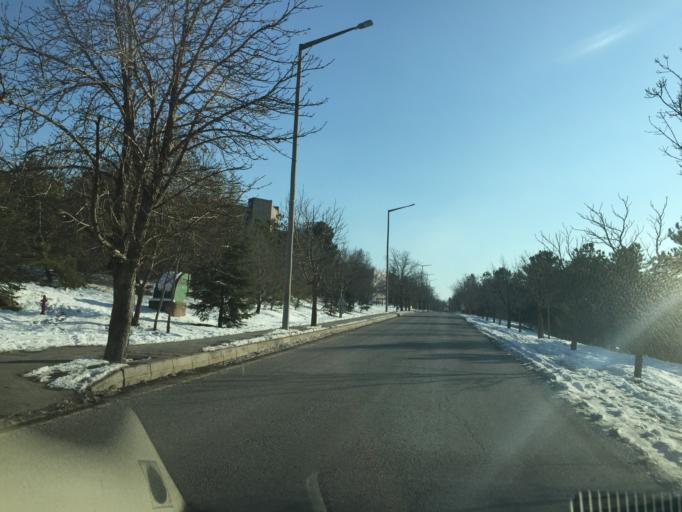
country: TR
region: Ankara
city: Ankara
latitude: 39.8920
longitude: 32.7811
